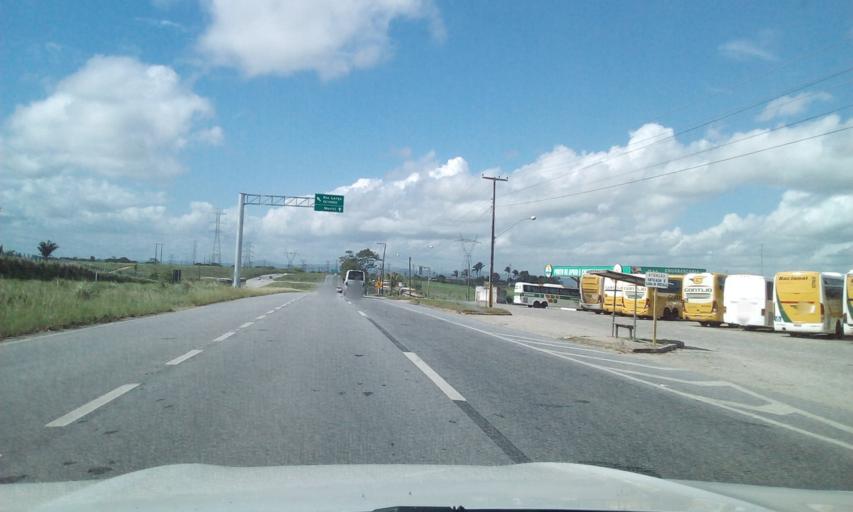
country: BR
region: Alagoas
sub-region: Messias
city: Messias
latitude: -9.4168
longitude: -35.8401
